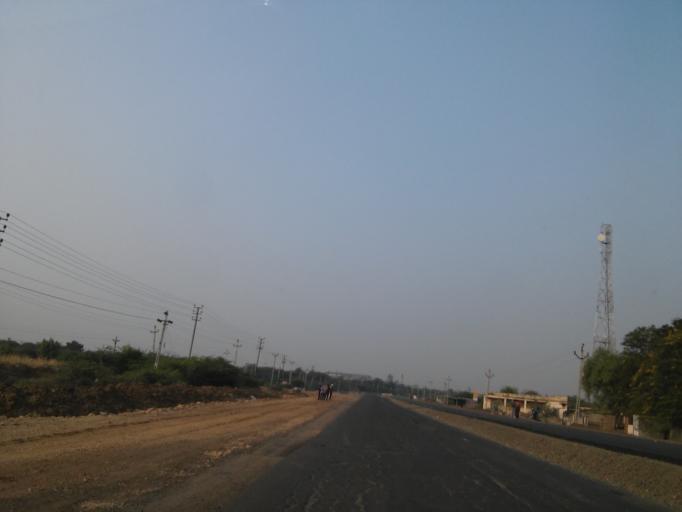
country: IN
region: Gujarat
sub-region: Kachchh
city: Bhachau
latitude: 23.3323
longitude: 70.2252
